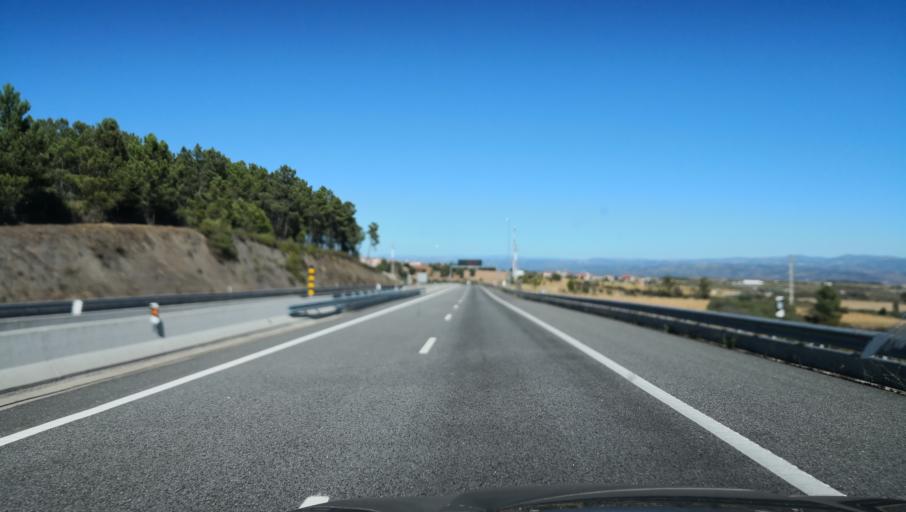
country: PT
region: Braganca
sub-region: Mirandela
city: Mirandela
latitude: 41.4547
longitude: -7.2665
